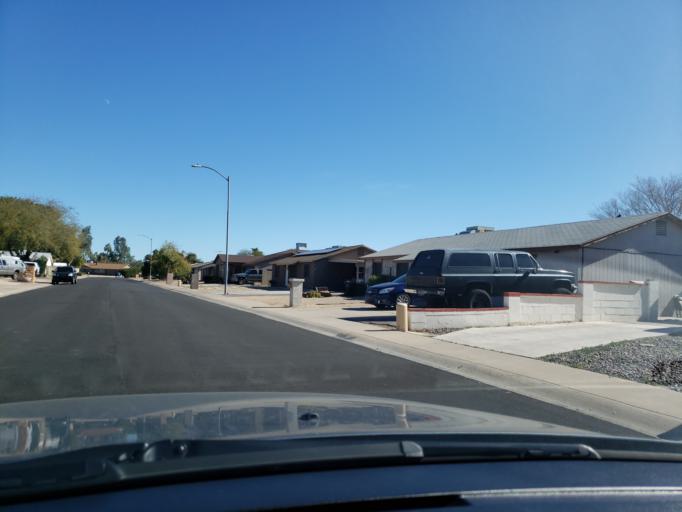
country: US
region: Arizona
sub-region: Maricopa County
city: Paradise Valley
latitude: 33.6147
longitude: -111.9942
